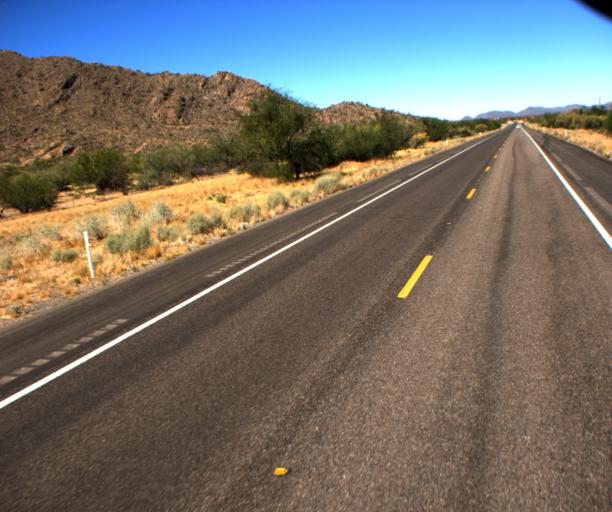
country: US
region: Arizona
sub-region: Pima County
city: Sells
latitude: 32.0104
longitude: -111.6612
